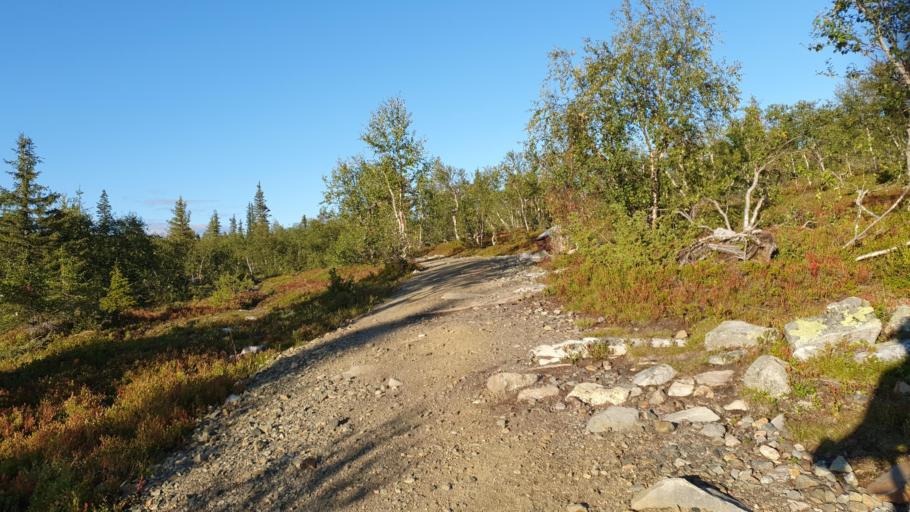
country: FI
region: Lapland
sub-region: Tunturi-Lappi
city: Kolari
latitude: 67.5830
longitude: 24.2356
